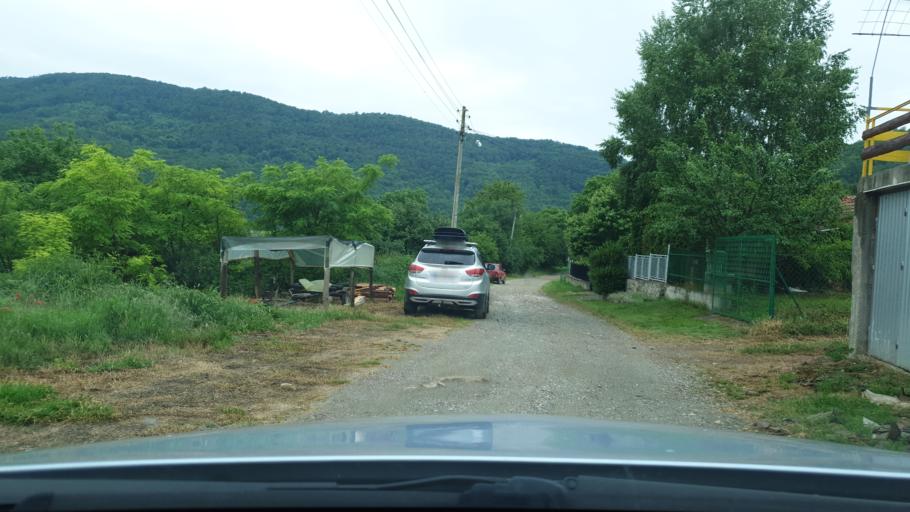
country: RS
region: Central Serbia
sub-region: Zajecarski Okrug
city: Soko Banja
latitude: 43.6594
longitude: 21.7626
